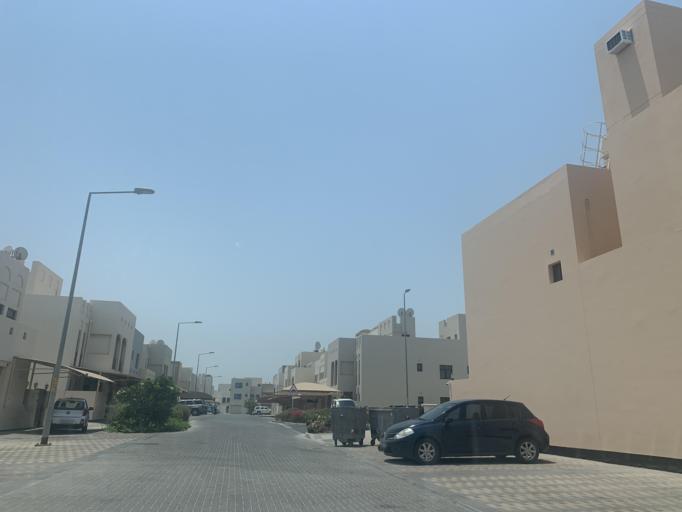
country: BH
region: Muharraq
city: Al Hadd
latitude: 26.2356
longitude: 50.6707
